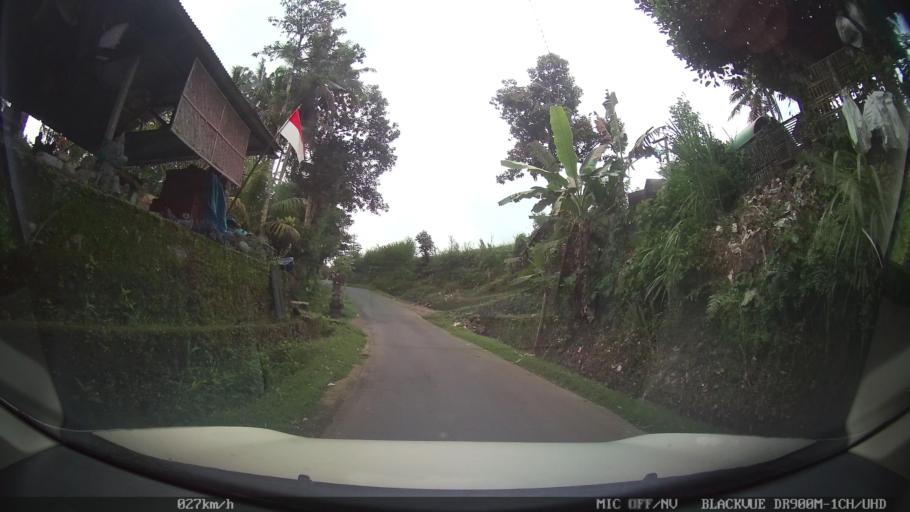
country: ID
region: Bali
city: Banjar Petak
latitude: -8.4451
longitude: 115.3226
